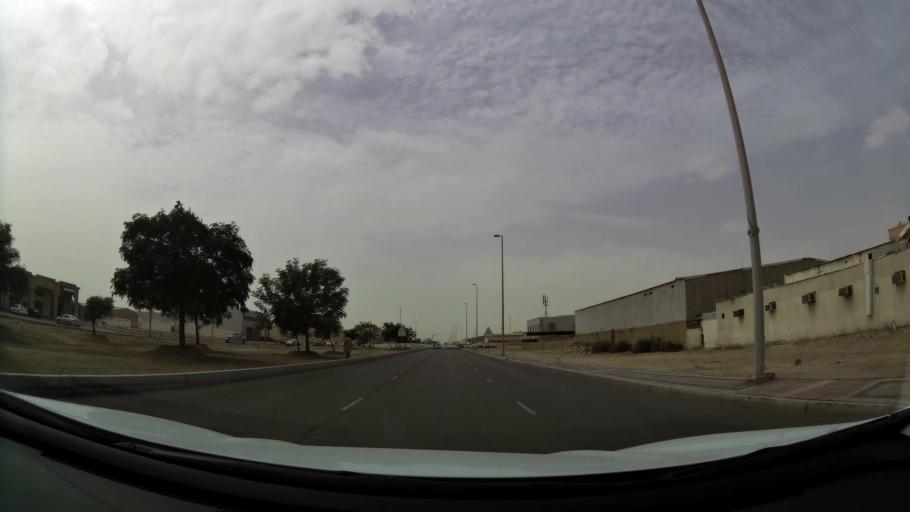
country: AE
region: Abu Dhabi
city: Abu Dhabi
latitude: 24.3685
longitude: 54.5032
